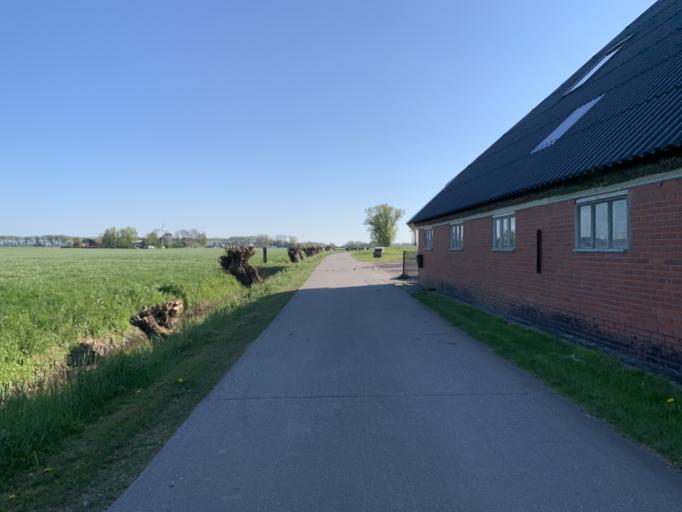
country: NL
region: Groningen
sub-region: Gemeente Winsum
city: Winsum
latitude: 53.2862
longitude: 6.5161
